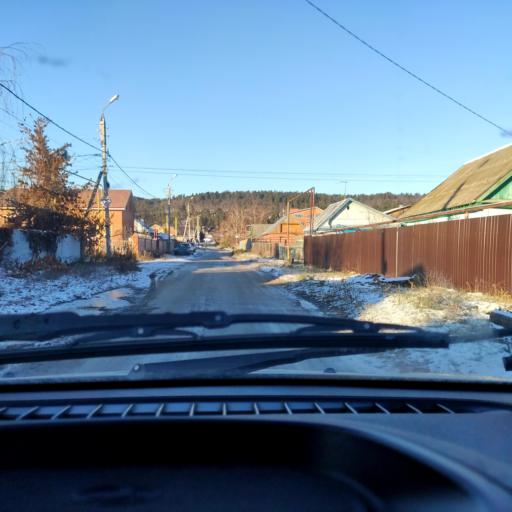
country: RU
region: Samara
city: Zhigulevsk
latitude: 53.4661
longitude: 49.6036
